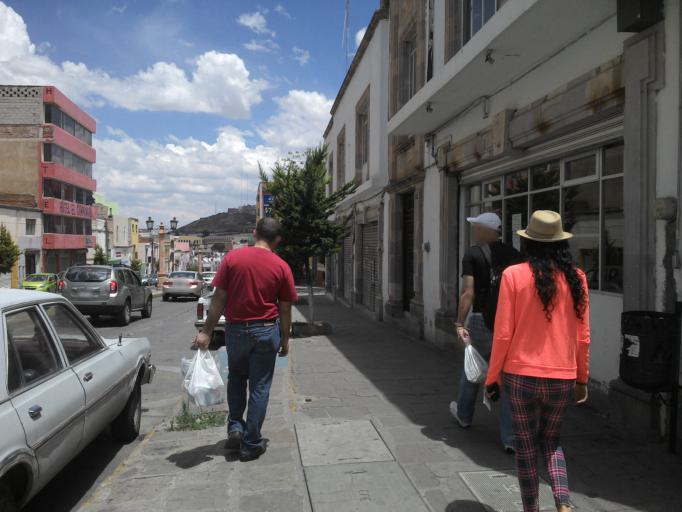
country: MX
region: Zacatecas
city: Zacatecas
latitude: 22.7708
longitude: -102.5710
